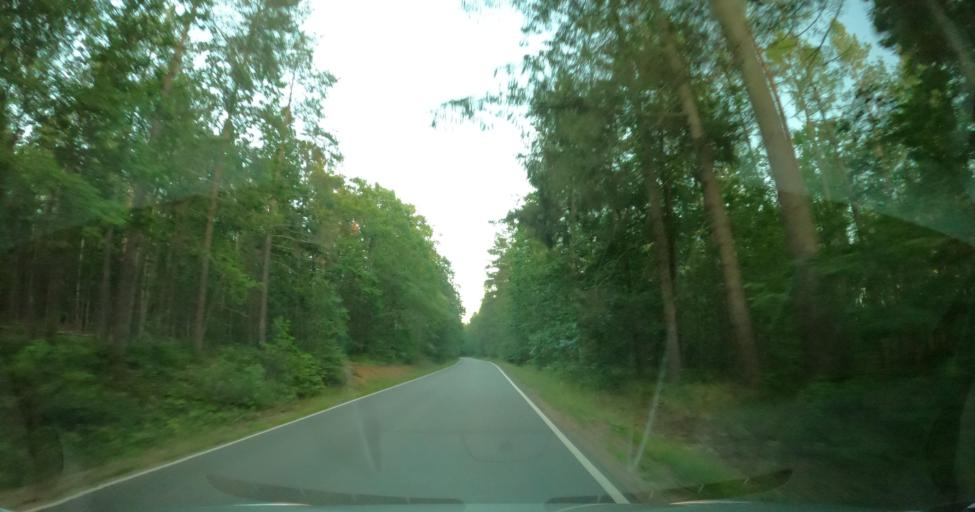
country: PL
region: Pomeranian Voivodeship
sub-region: Powiat leborski
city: Lebork
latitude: 54.5036
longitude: 17.8195
